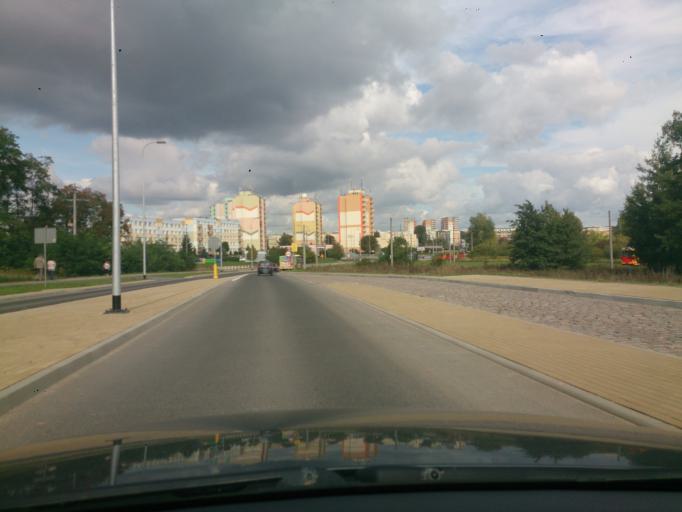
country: PL
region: Kujawsko-Pomorskie
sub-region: Grudziadz
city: Grudziadz
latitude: 53.4483
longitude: 18.7154
